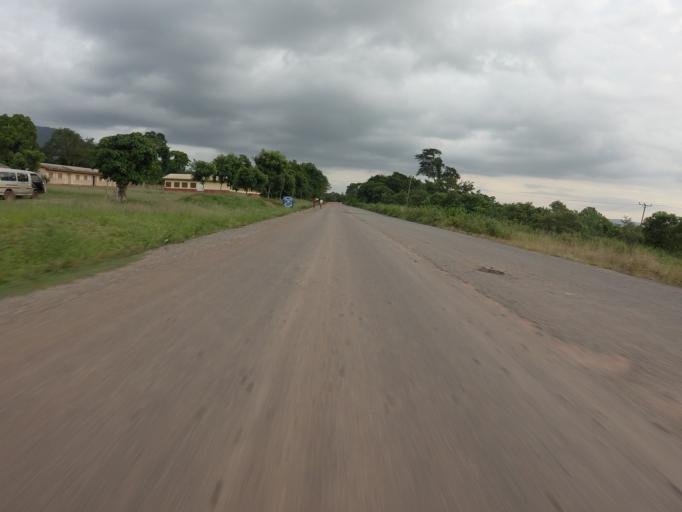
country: GH
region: Volta
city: Kpandu
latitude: 6.8183
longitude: 0.3747
